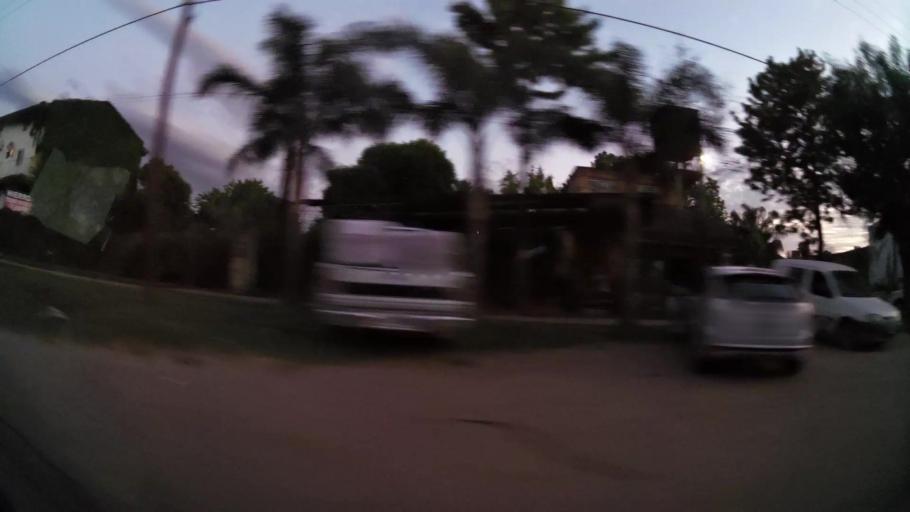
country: AR
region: Buenos Aires
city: Santa Catalina - Dique Lujan
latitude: -34.4665
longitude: -58.7497
